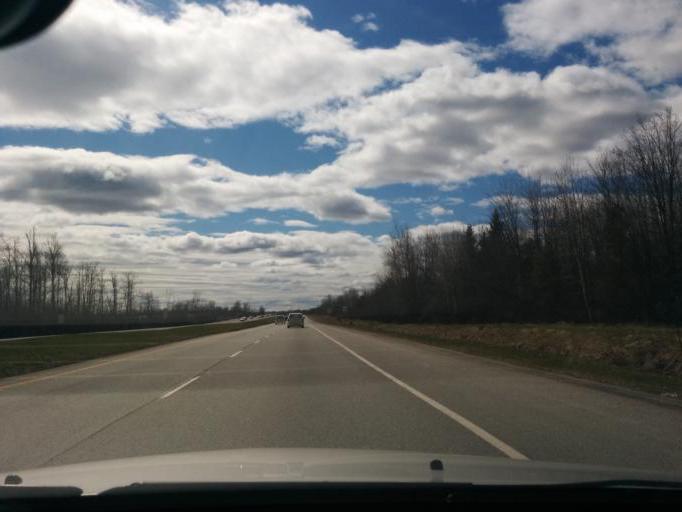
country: CA
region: Ontario
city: Bells Corners
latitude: 45.4154
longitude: -75.8112
